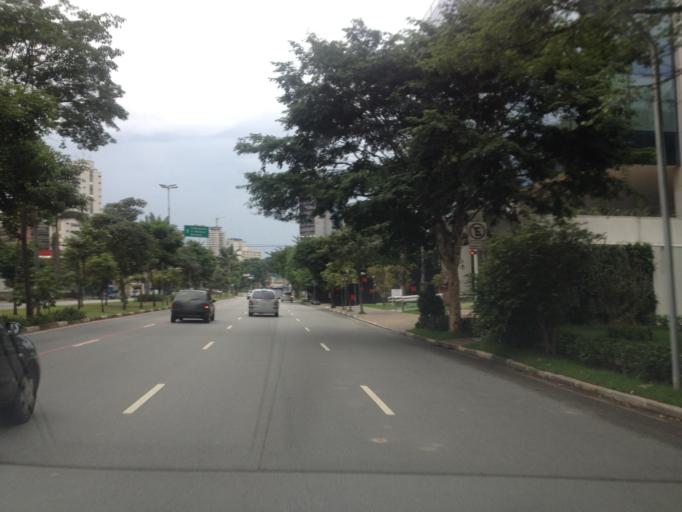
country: BR
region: Sao Paulo
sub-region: Sao Paulo
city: Sao Paulo
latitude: -23.5948
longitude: -46.6803
